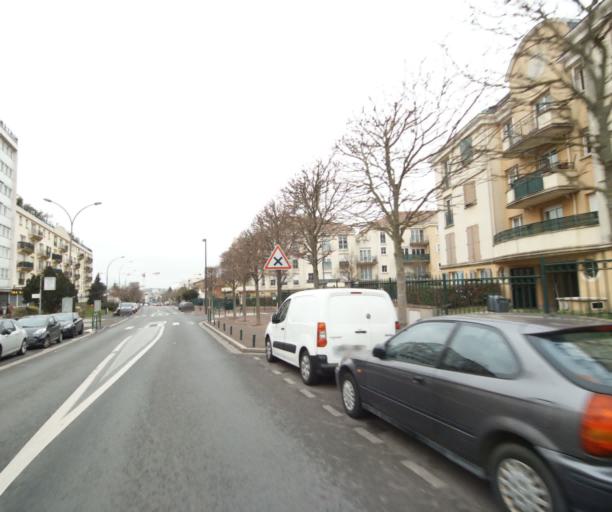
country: FR
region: Ile-de-France
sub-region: Departement des Hauts-de-Seine
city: Rueil-Malmaison
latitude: 48.8676
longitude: 2.1970
